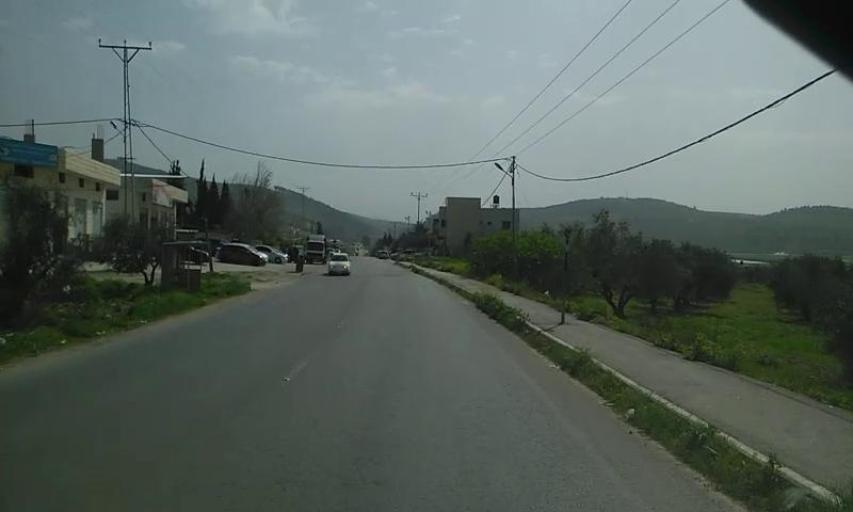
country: PS
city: Bir al Basha
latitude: 32.4176
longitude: 35.2297
